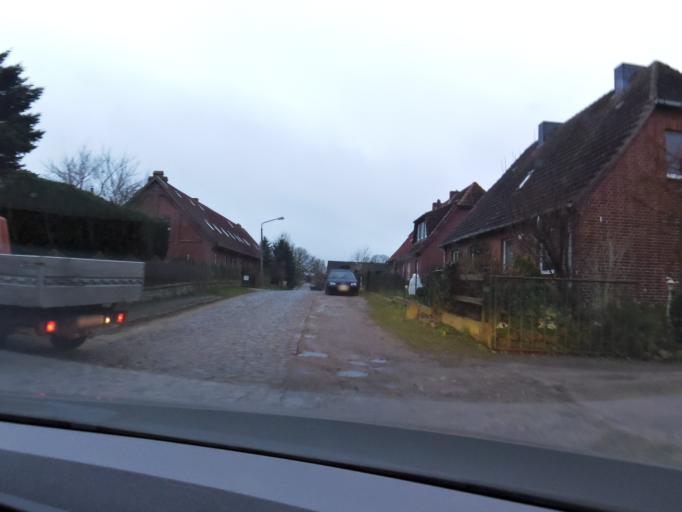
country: DE
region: Mecklenburg-Vorpommern
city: Roggendorf
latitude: 53.6879
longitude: 10.9967
